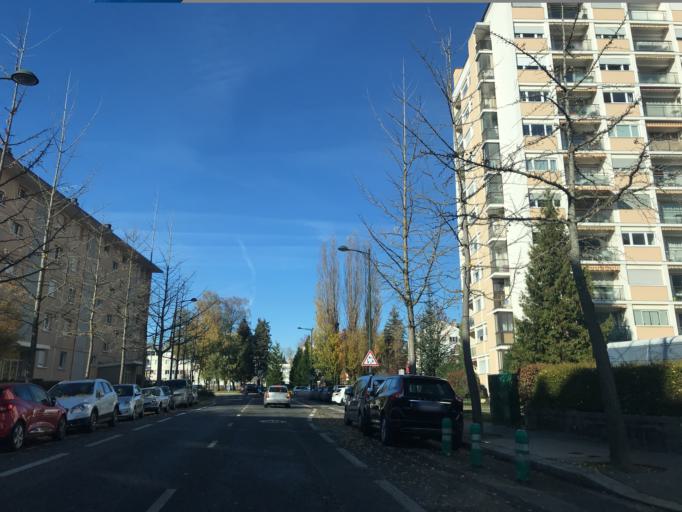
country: FR
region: Rhone-Alpes
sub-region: Departement de la Haute-Savoie
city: Annecy-le-Vieux
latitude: 45.9110
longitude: 6.1326
